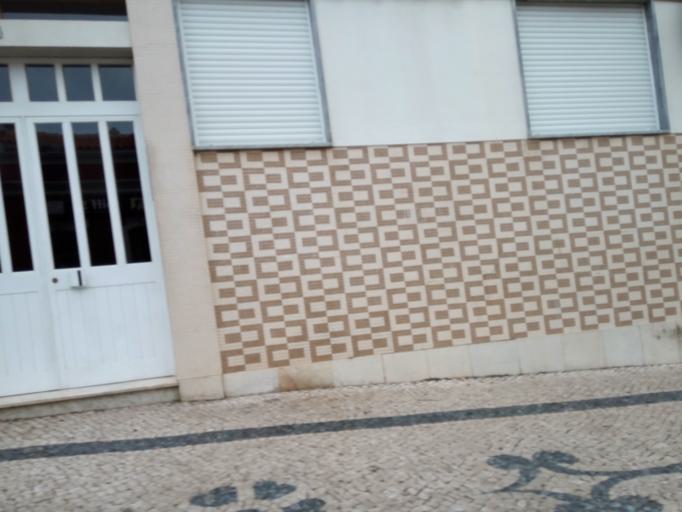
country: PT
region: Faro
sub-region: Loule
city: Loule
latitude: 37.1363
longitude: -8.0223
